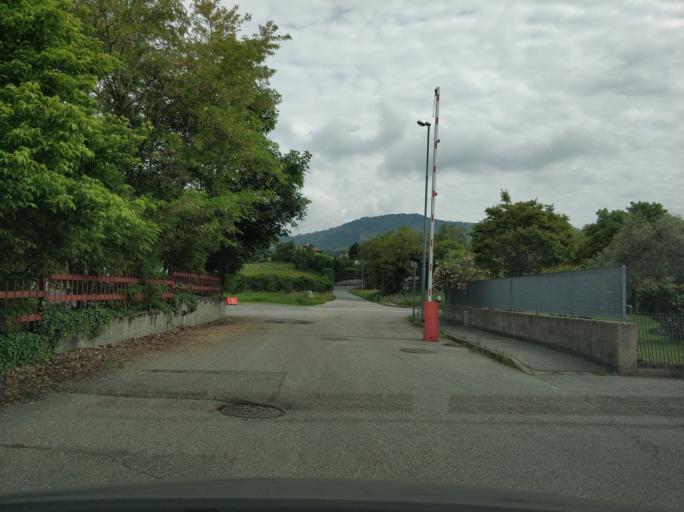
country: IT
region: Piedmont
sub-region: Provincia di Torino
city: Balangero
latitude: 45.2687
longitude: 7.5016
